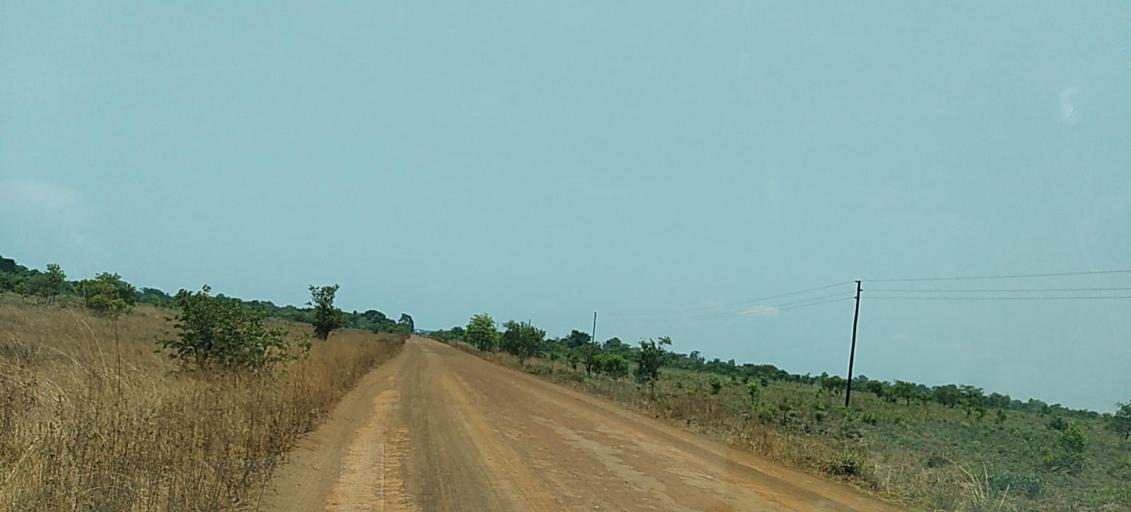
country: ZM
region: Copperbelt
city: Mpongwe
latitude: -13.6811
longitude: 27.8582
